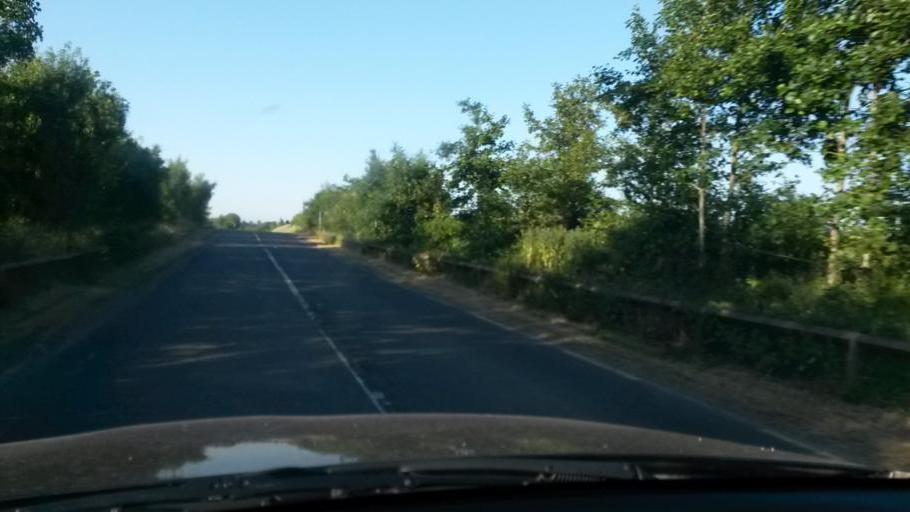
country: IE
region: Leinster
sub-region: Fingal County
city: Blanchardstown
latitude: 53.4373
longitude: -6.3555
